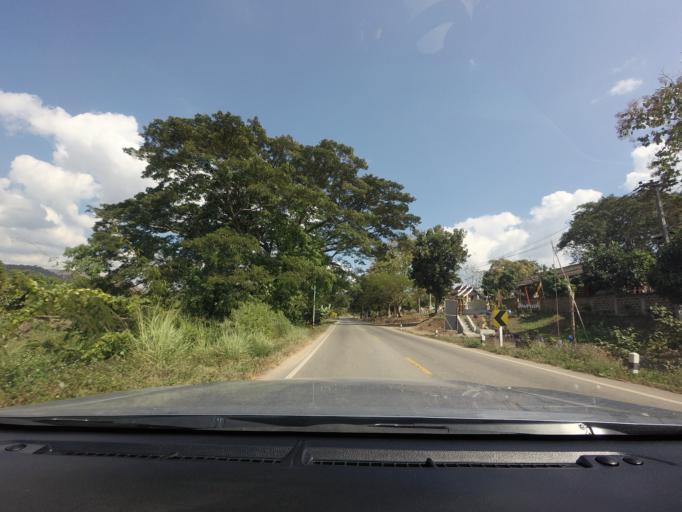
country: TH
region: Chiang Mai
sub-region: Amphoe Chiang Dao
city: Chiang Dao
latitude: 19.4827
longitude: 99.0238
